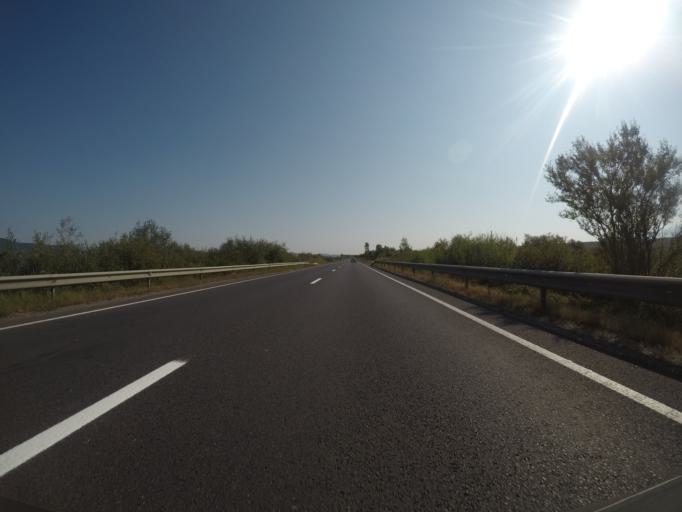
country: RO
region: Sibiu
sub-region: Comuna Porumbacu de Jos
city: Porumbacu de Jos
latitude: 45.7514
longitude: 24.4300
